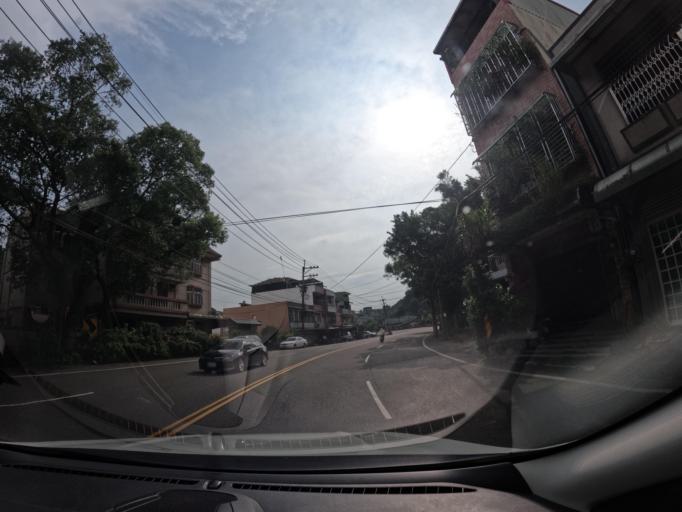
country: TW
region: Taiwan
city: Daxi
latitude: 24.8950
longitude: 121.3193
